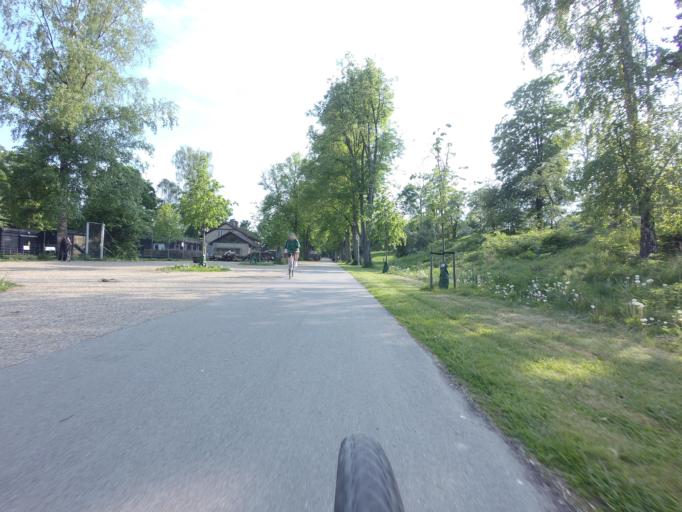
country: DK
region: Capital Region
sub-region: Rodovre Kommune
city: Rodovre
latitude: 55.6891
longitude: 12.4365
